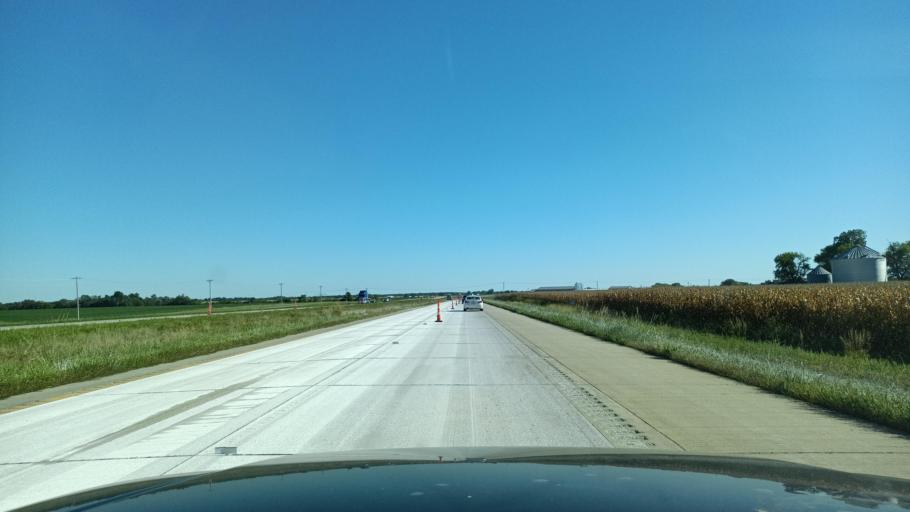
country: US
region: Missouri
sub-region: Randolph County
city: Moberly
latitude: 39.5234
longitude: -92.4390
